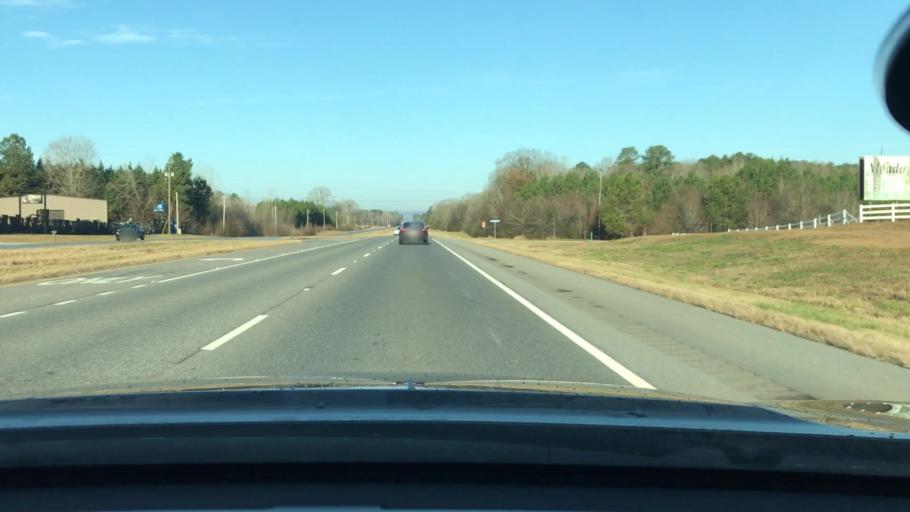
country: US
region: Alabama
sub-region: Shelby County
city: Harpersville
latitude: 33.3201
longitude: -86.3990
